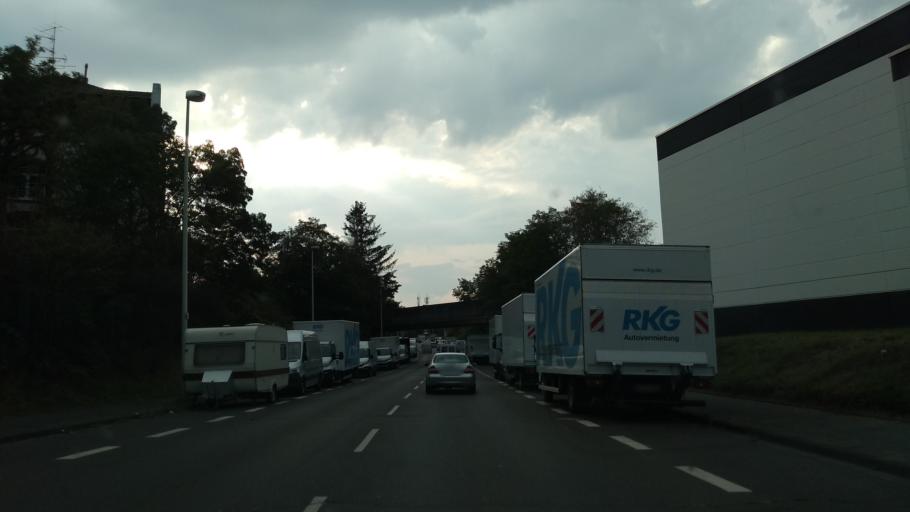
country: DE
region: North Rhine-Westphalia
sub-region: Regierungsbezirk Koln
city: Bonn
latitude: 50.7390
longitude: 7.0641
